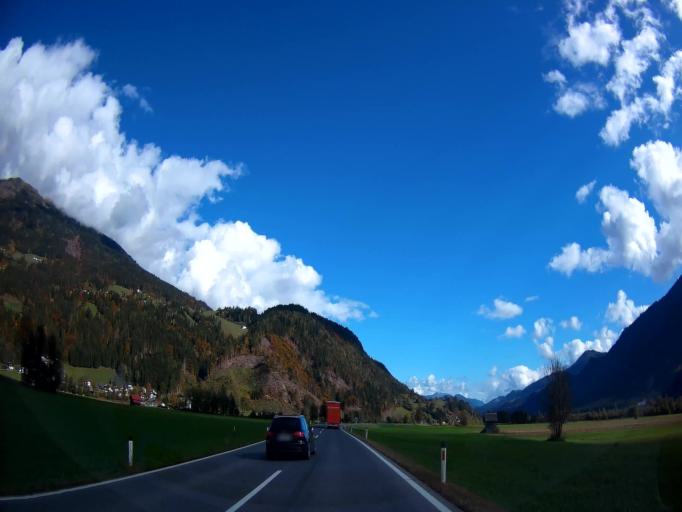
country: AT
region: Carinthia
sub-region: Politischer Bezirk Spittal an der Drau
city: Irschen
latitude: 46.7408
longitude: 13.0381
